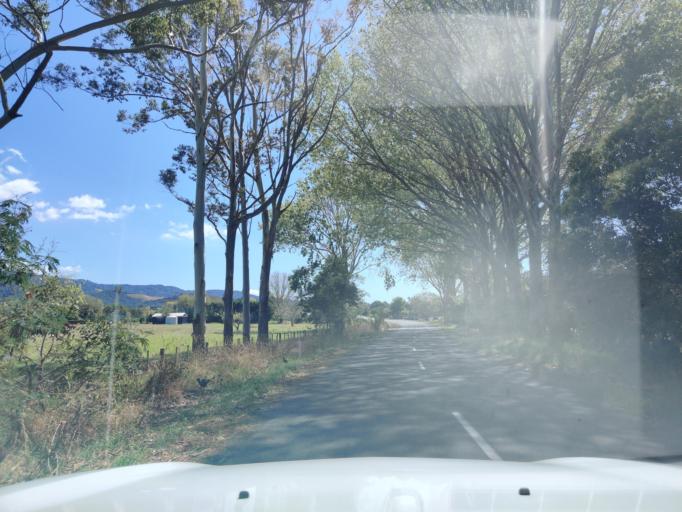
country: NZ
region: Waikato
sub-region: Thames-Coromandel District
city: Thames
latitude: -37.0516
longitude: 175.3006
